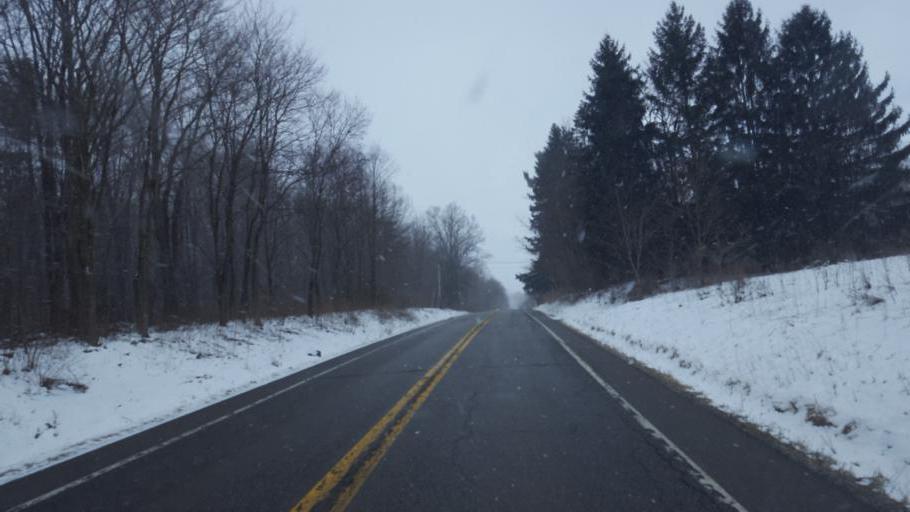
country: US
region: Pennsylvania
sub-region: Crawford County
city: Cochranton
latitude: 41.4337
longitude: -80.0747
